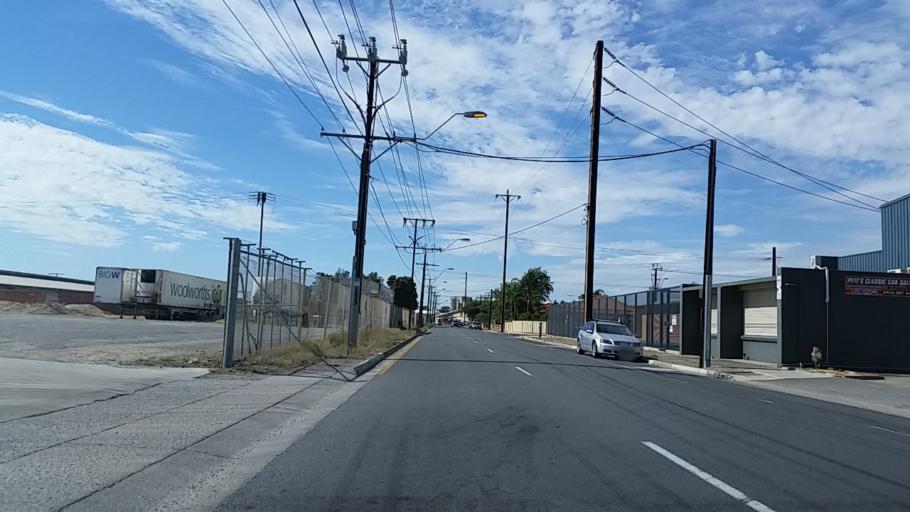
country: AU
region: South Australia
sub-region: Port Adelaide Enfield
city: Alberton
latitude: -34.8537
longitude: 138.5380
